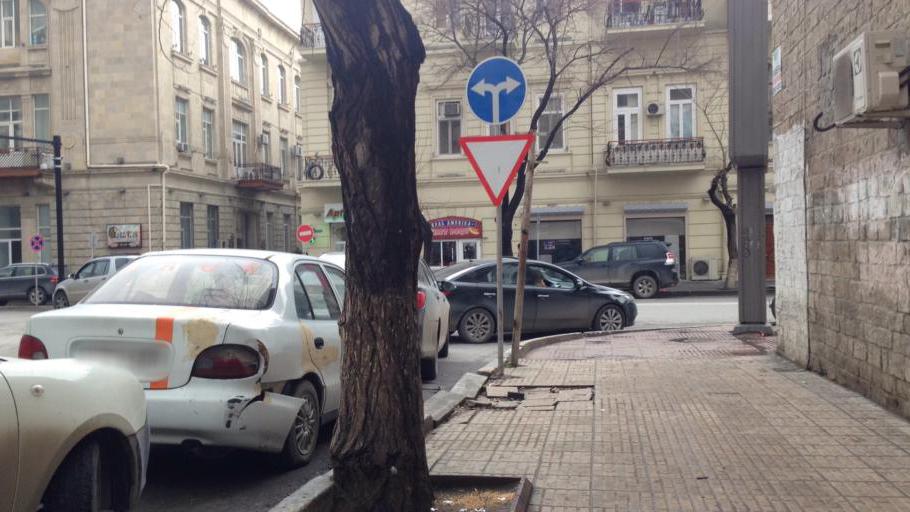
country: AZ
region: Baki
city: Baku
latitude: 40.3777
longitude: 49.8463
